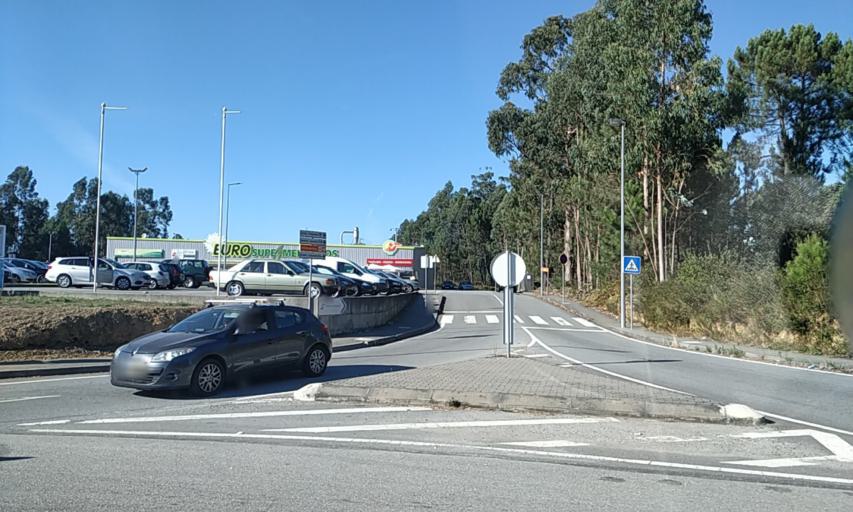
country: PT
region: Porto
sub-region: Valongo
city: Alfena
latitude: 41.2605
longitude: -8.4896
